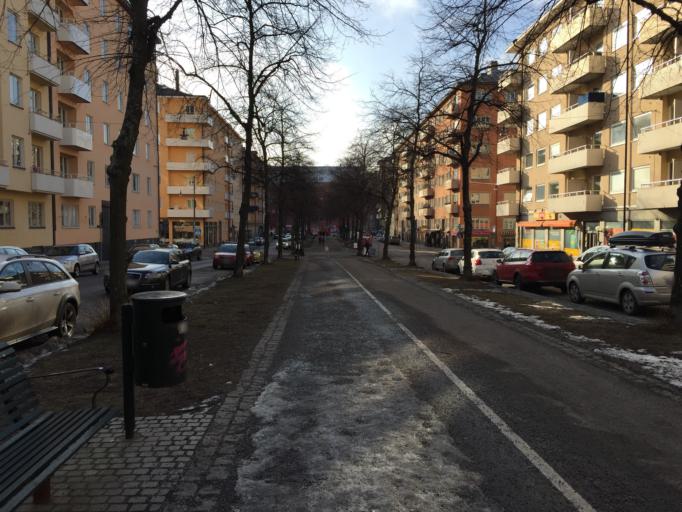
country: SE
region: Stockholm
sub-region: Stockholms Kommun
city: OEstermalm
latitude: 59.3426
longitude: 18.0916
